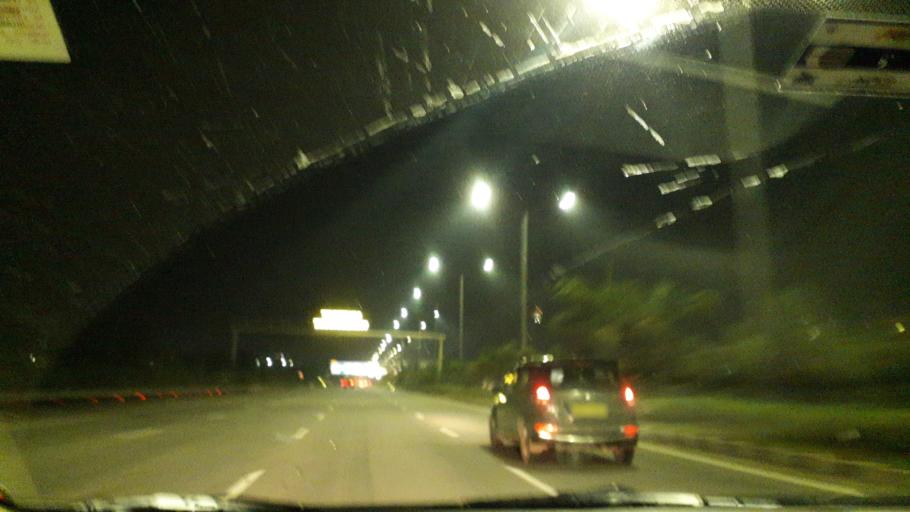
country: IN
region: Telangana
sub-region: Hyderabad
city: Hyderabad
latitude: 17.3365
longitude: 78.3679
